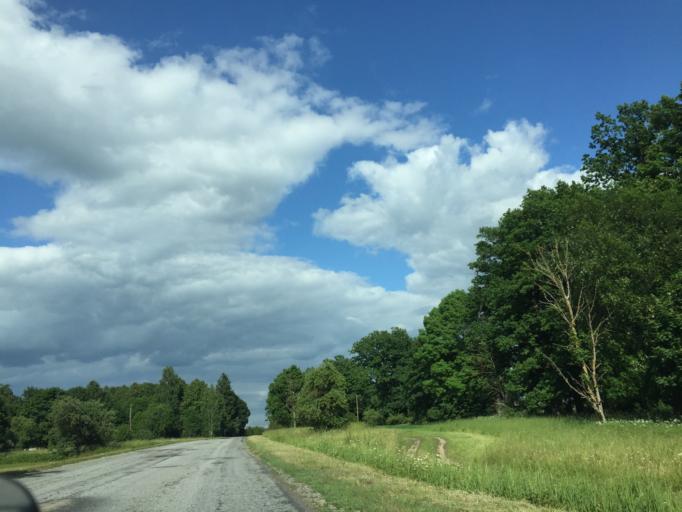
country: LV
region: Ogre
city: Jumprava
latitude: 56.7976
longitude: 25.0476
